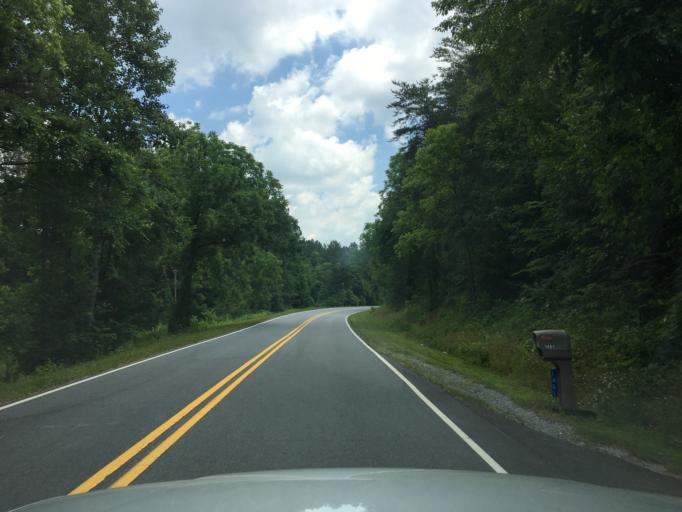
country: US
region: North Carolina
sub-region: Rutherford County
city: Rutherfordton
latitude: 35.3503
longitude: -82.0015
